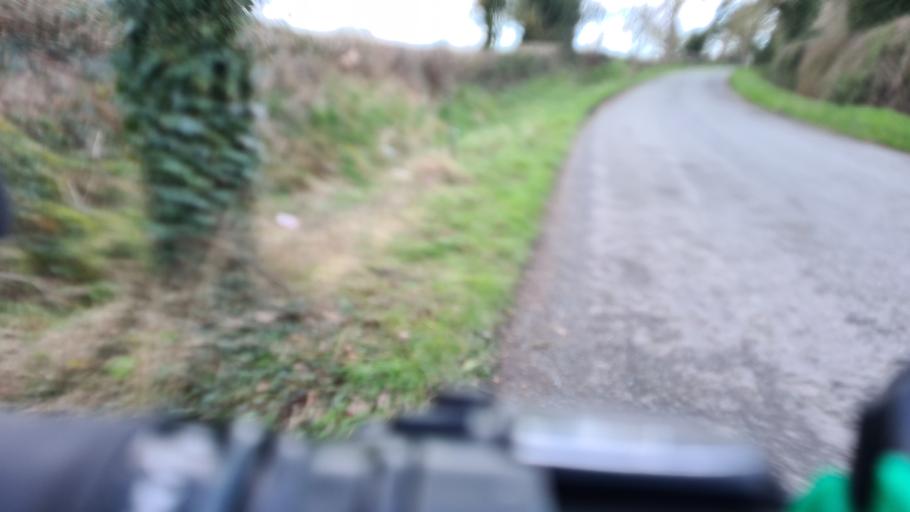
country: IE
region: Leinster
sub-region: Kildare
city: Maynooth
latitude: 53.3494
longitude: -6.5855
